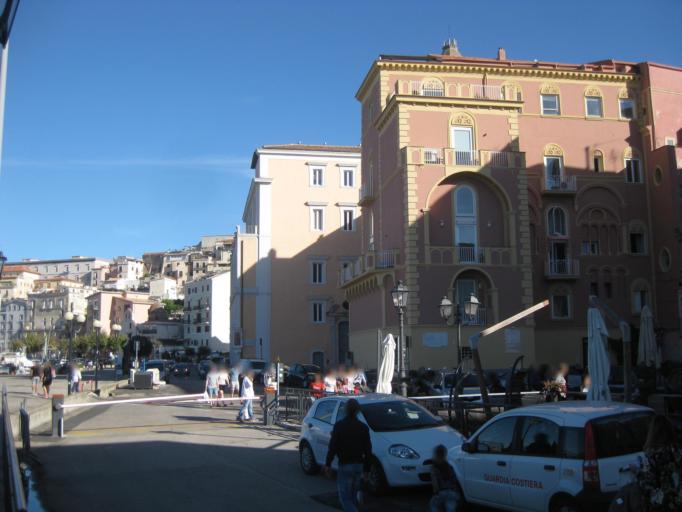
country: IT
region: Latium
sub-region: Provincia di Latina
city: Gaeta
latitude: 41.2097
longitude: 13.5861
